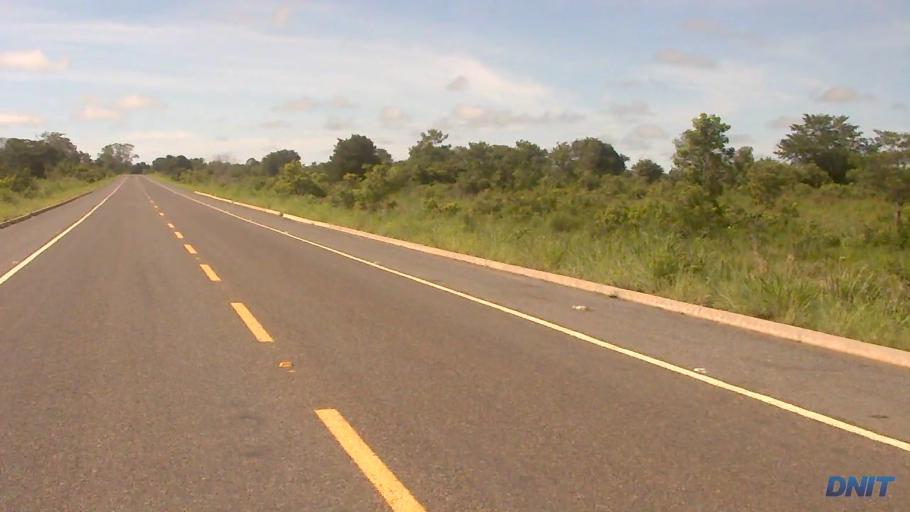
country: BR
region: Goias
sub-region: Sao Miguel Do Araguaia
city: Sao Miguel do Araguaia
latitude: -13.3062
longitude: -50.1731
